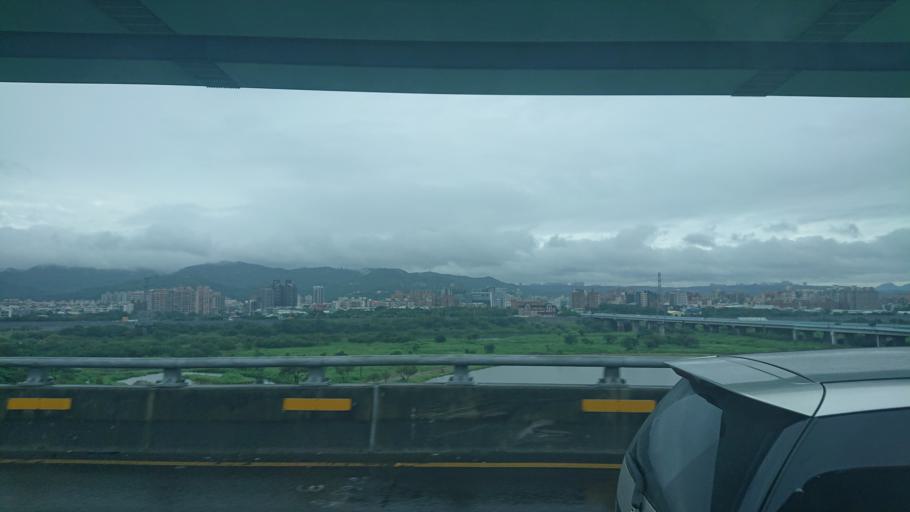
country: TW
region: Taipei
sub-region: Taipei
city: Banqiao
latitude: 24.9738
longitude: 121.4330
